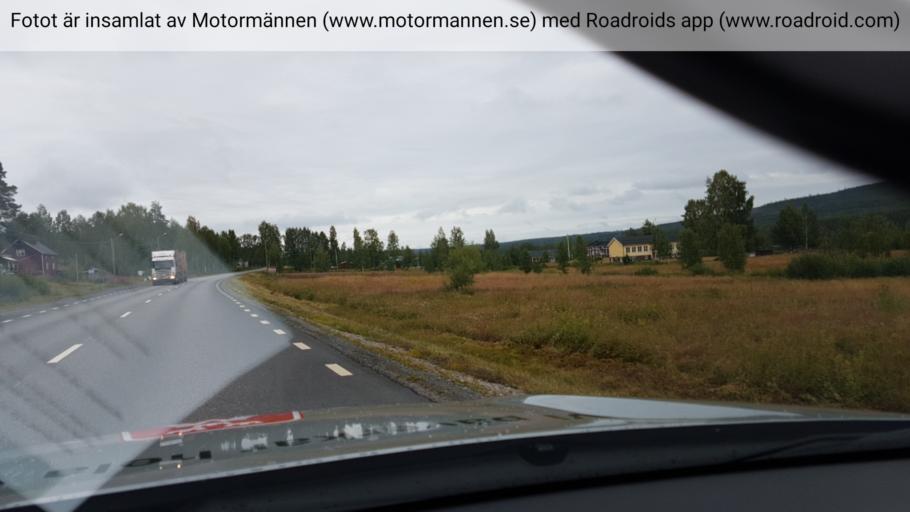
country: SE
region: Norrbotten
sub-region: Alvsbyns Kommun
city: AElvsbyn
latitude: 66.2848
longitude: 20.8189
